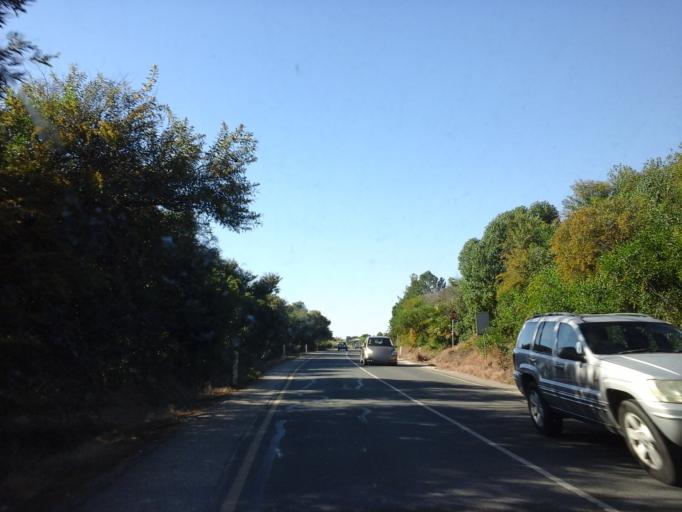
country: CY
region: Pafos
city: Polis
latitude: 34.9976
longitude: 32.4459
